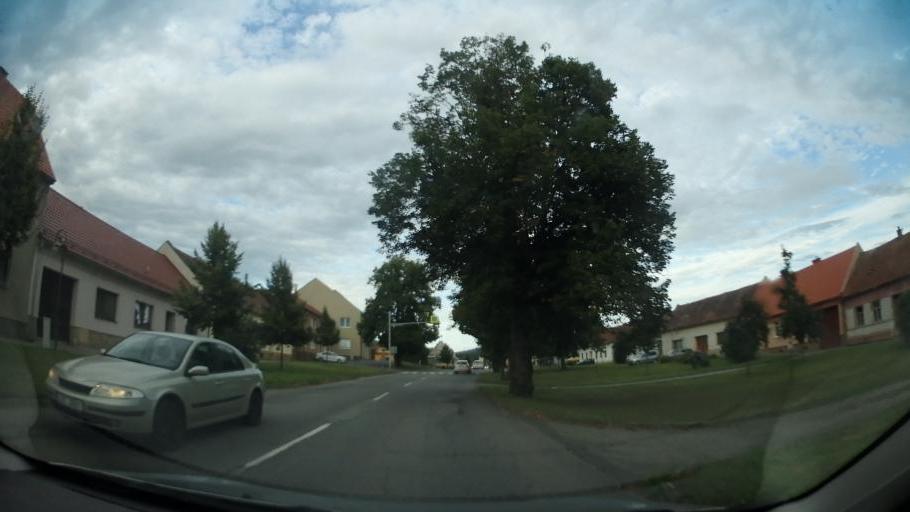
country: CZ
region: South Moravian
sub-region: Okres Blansko
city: Boskovice
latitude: 49.5389
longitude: 16.6931
